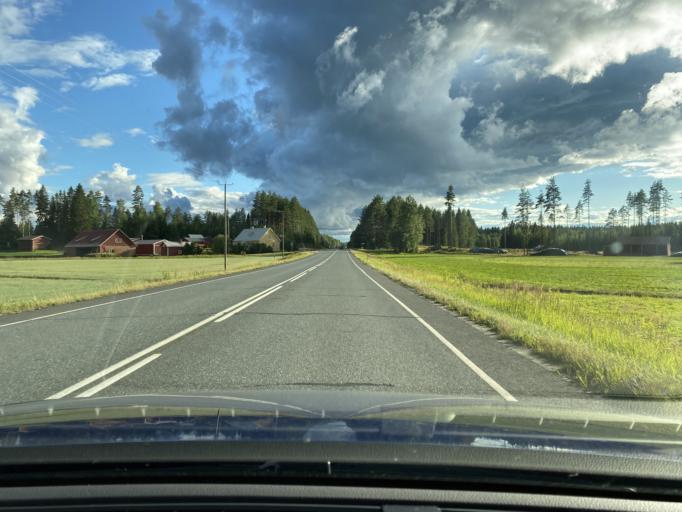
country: FI
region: Haeme
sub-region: Haemeenlinna
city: Renko
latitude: 60.8760
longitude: 24.2230
